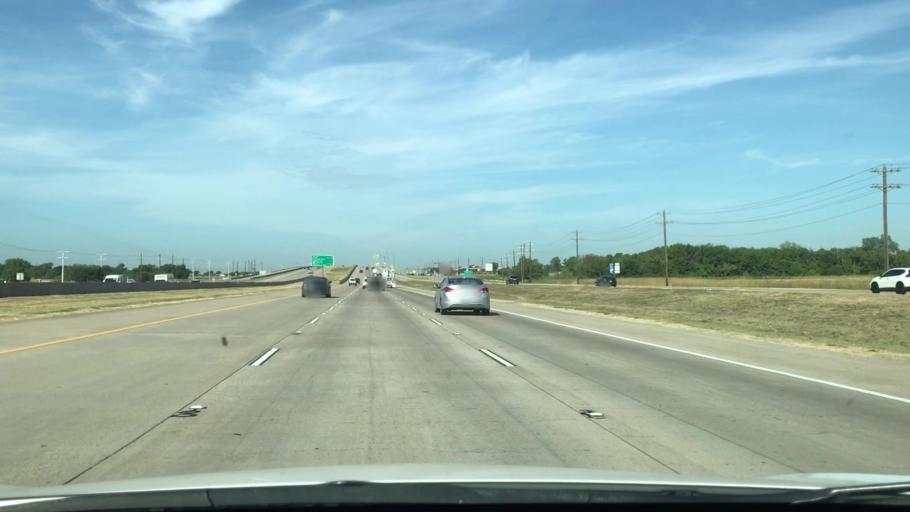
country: US
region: Texas
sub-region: Collin County
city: Allen
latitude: 33.1432
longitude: -96.6836
